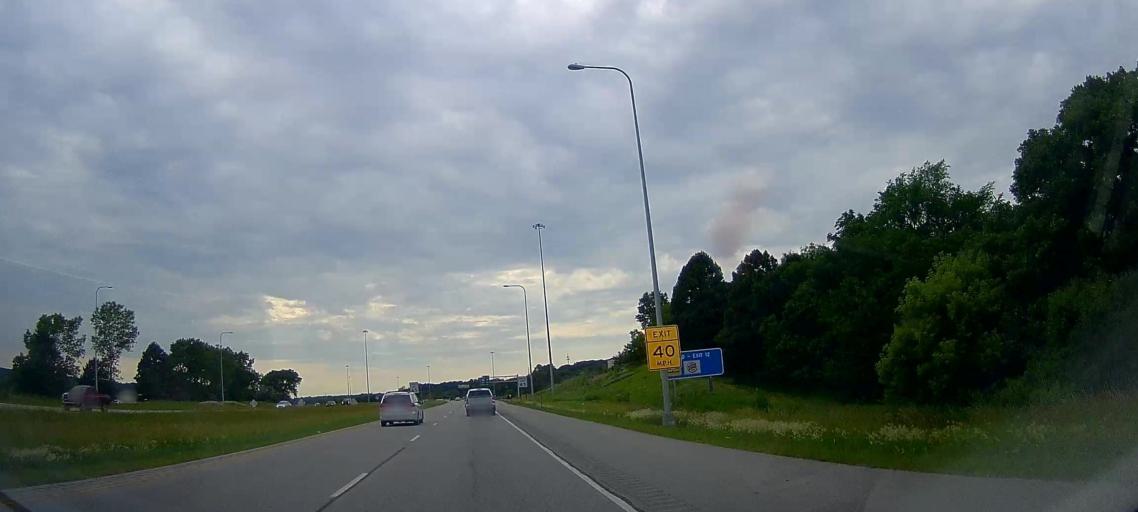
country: US
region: Iowa
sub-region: Pottawattamie County
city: Carter Lake
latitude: 41.3463
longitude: -95.9757
